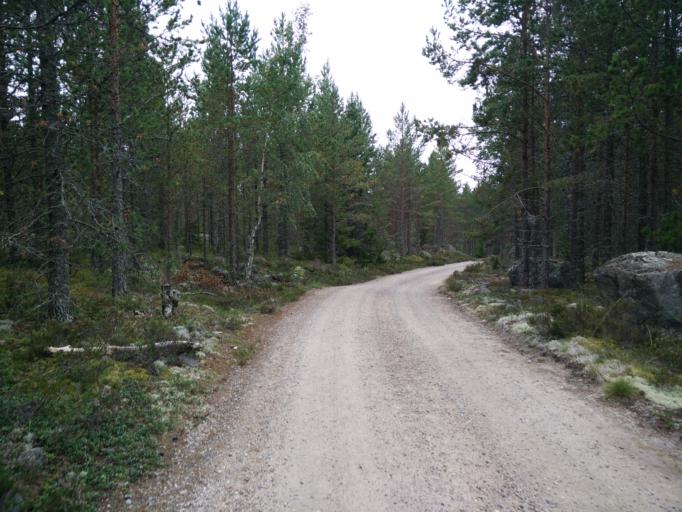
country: SE
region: Gaevleborg
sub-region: Hudiksvalls Kommun
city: Hudiksvall
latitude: 61.8350
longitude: 17.3397
